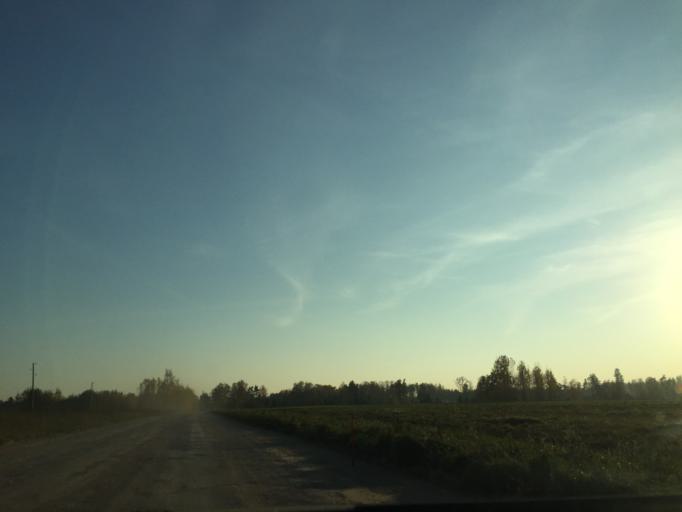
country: LV
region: Vainode
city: Vainode
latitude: 56.5472
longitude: 21.8389
